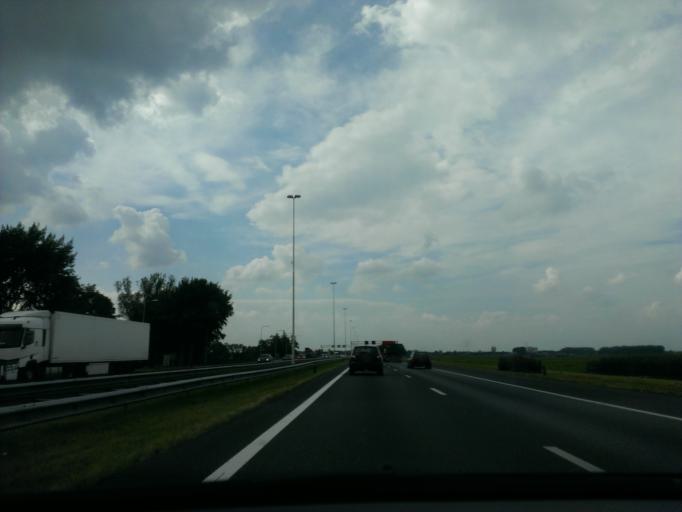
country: NL
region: Utrecht
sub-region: Gemeente Amersfoort
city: Hoogland
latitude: 52.2127
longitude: 5.3400
